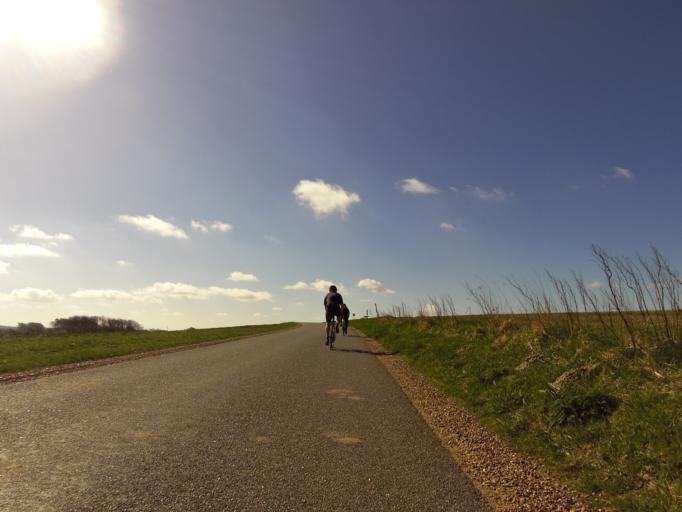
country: DK
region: Central Jutland
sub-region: Holstebro Kommune
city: Vinderup
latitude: 56.4631
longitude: 8.7220
